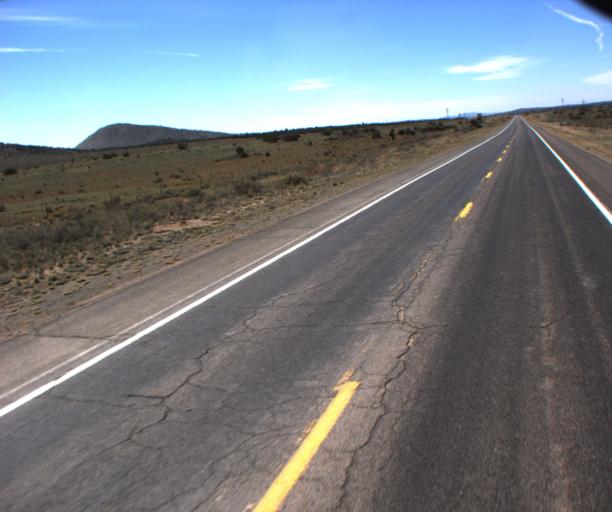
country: US
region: Arizona
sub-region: Mohave County
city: Peach Springs
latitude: 35.5423
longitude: -113.2756
